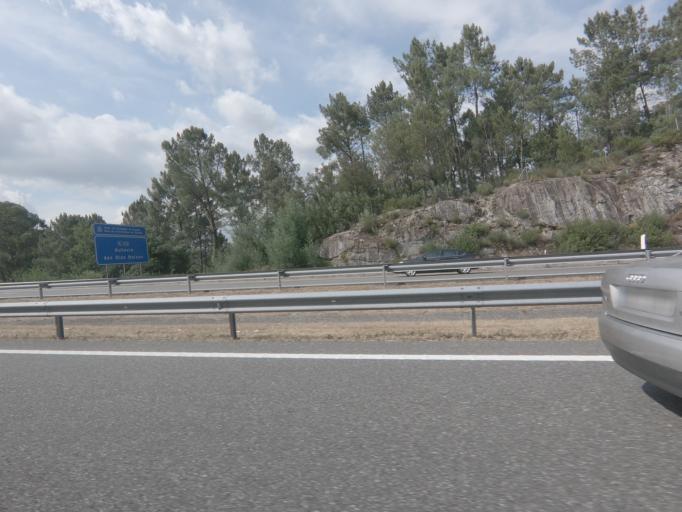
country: ES
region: Galicia
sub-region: Provincia de Ourense
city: Ribadavia
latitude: 42.3017
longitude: -8.1387
